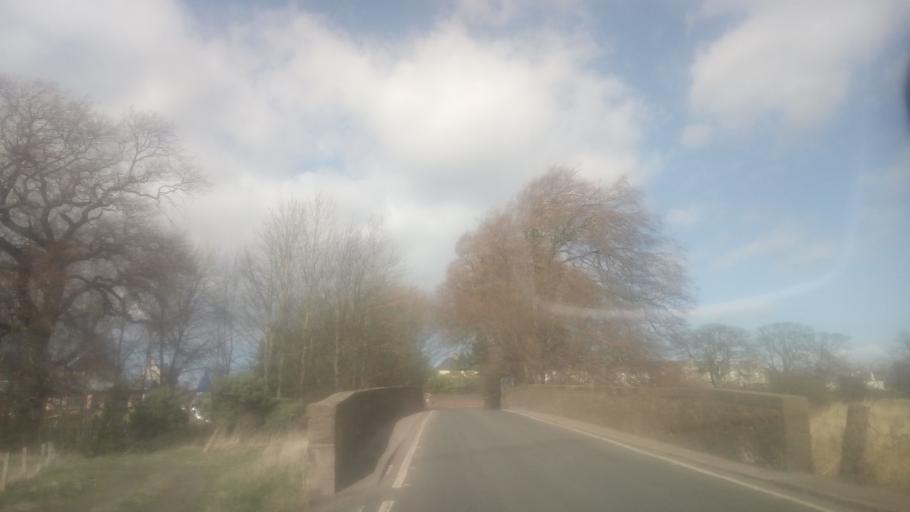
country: GB
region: Scotland
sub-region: East Lothian
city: Ormiston
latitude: 55.9096
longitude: -2.9407
